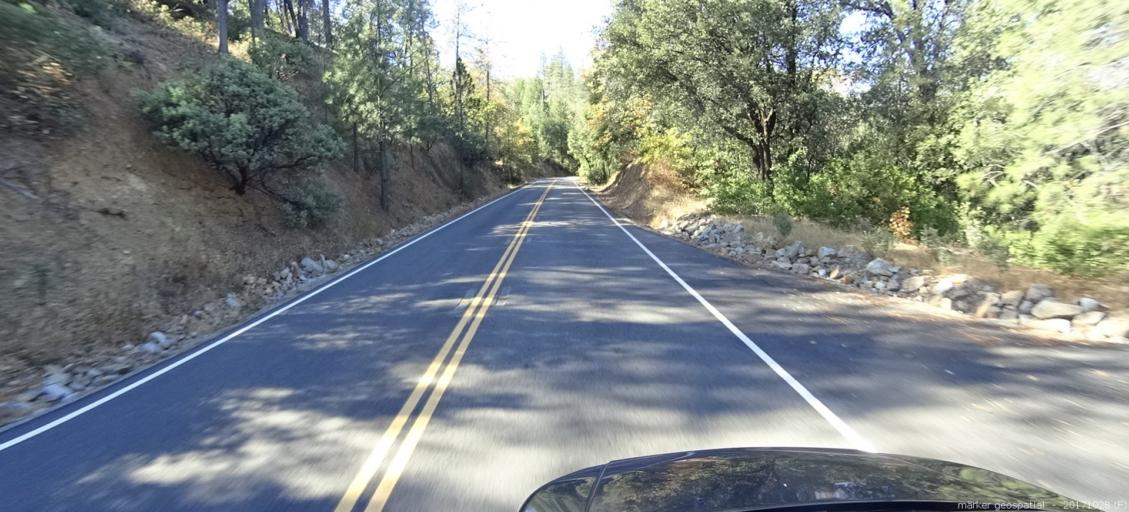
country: US
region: California
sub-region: Shasta County
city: Shasta
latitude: 40.6031
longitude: -122.5510
